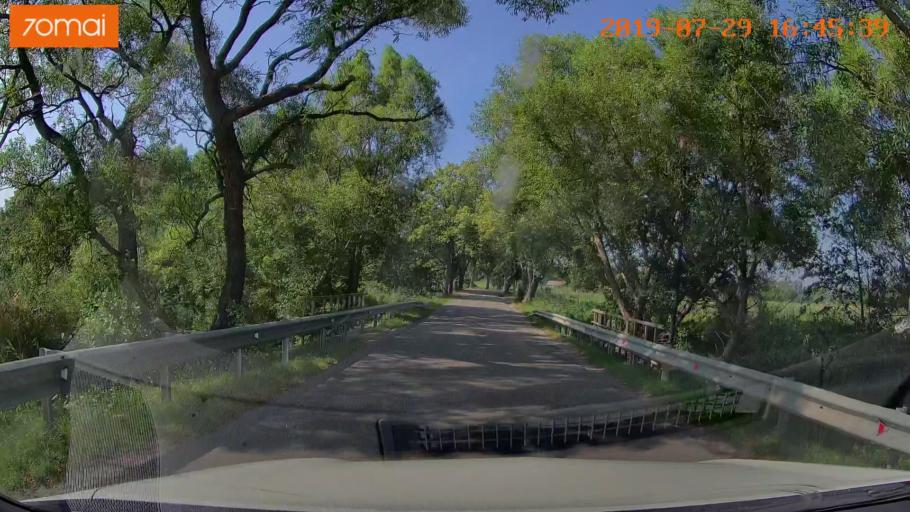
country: RU
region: Kaliningrad
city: Primorsk
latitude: 54.7668
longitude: 20.0796
